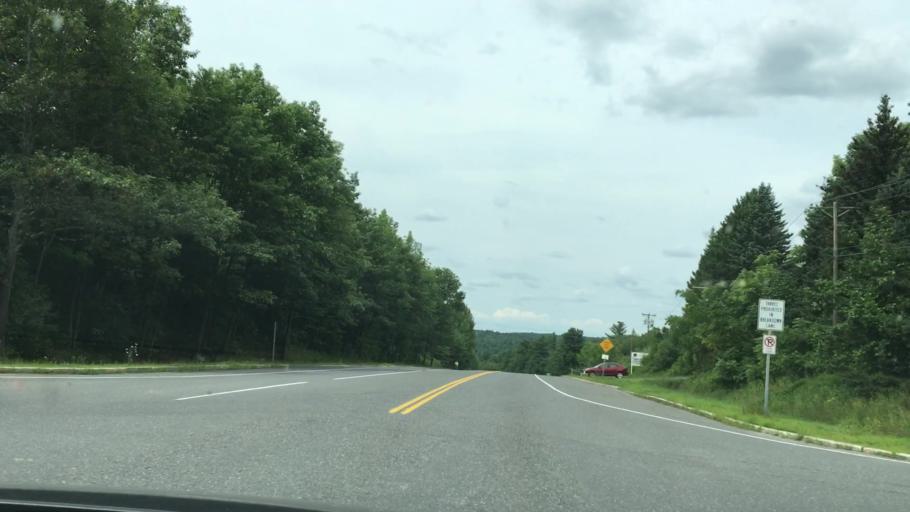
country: US
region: Massachusetts
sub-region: Worcester County
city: Gardner
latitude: 42.5983
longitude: -71.9883
